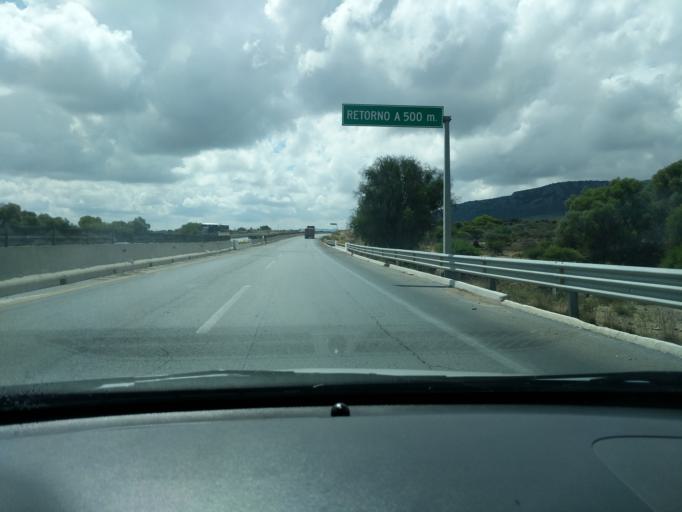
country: MX
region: Zacatecas
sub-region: Pinos
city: Santiago
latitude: 22.4069
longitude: -101.3929
